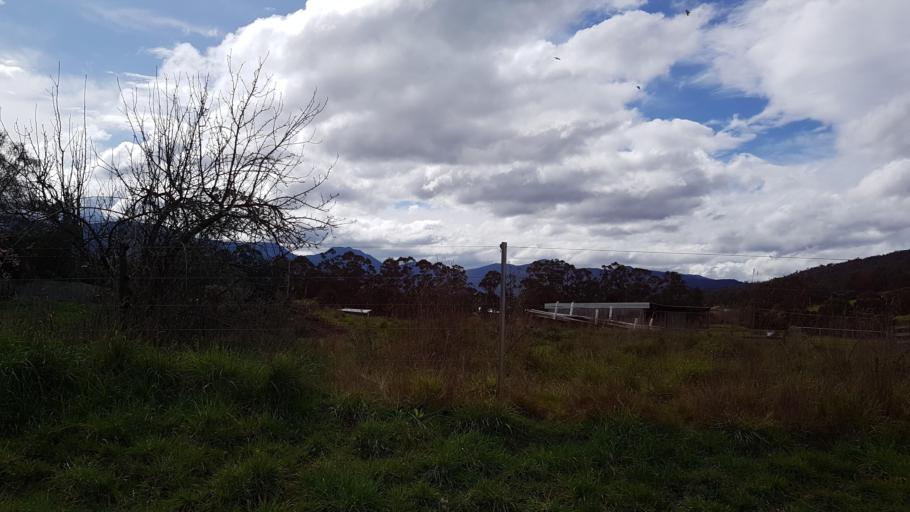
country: AU
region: Tasmania
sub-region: Huon Valley
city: Huonville
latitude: -43.0010
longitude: 147.0675
